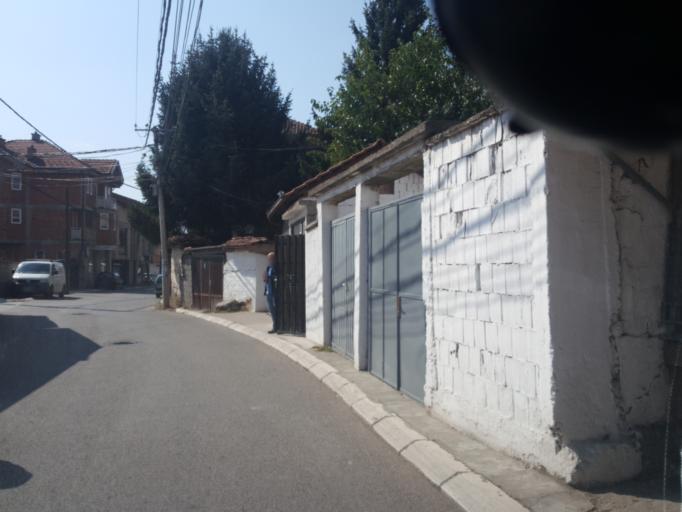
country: XK
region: Gjakova
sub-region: Komuna e Gjakoves
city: Gjakove
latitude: 42.3804
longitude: 20.4344
